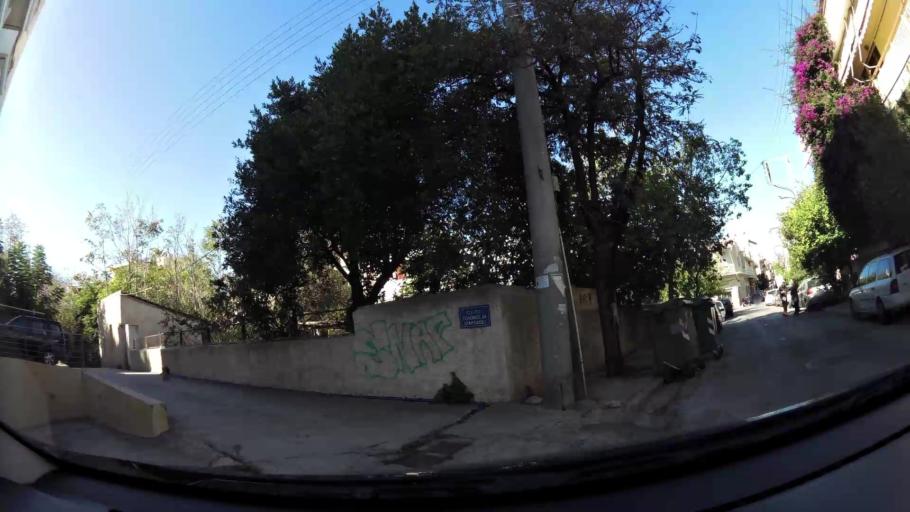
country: GR
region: Attica
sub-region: Nomarchia Athinas
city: Khalandrion
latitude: 38.0183
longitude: 23.7990
